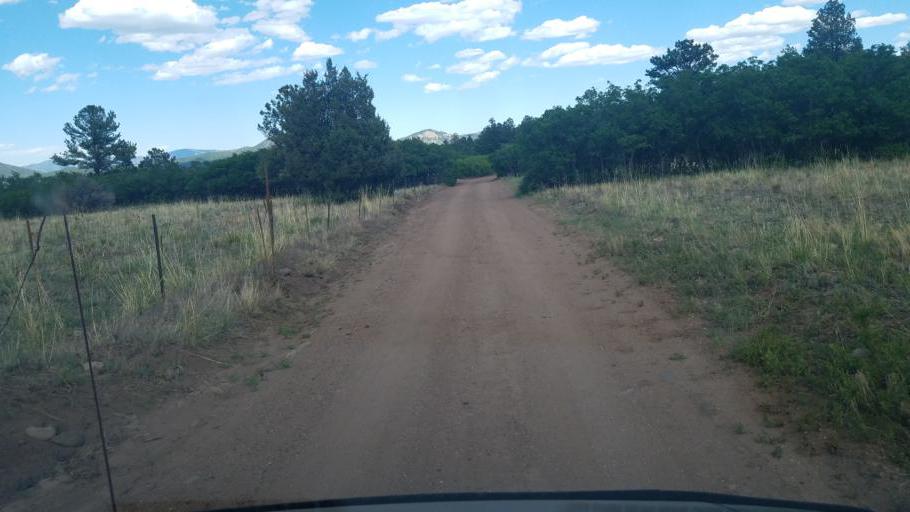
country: US
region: Colorado
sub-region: Custer County
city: Westcliffe
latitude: 38.2217
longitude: -105.6058
